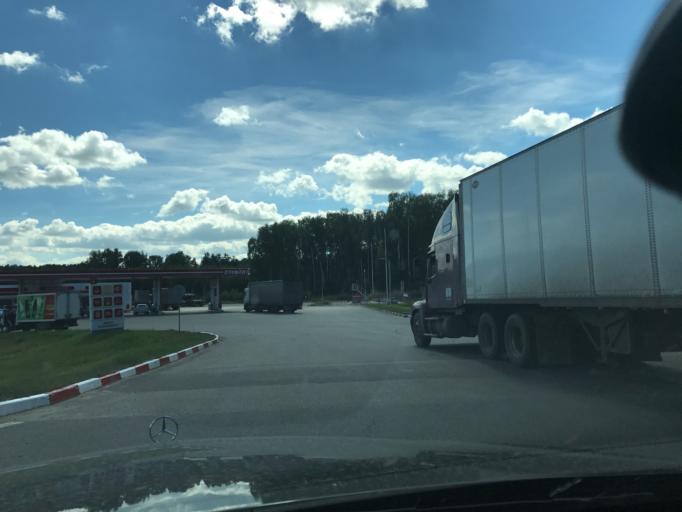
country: RU
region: Nizjnij Novgorod
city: Gorbatovka
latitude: 56.2433
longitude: 43.7218
